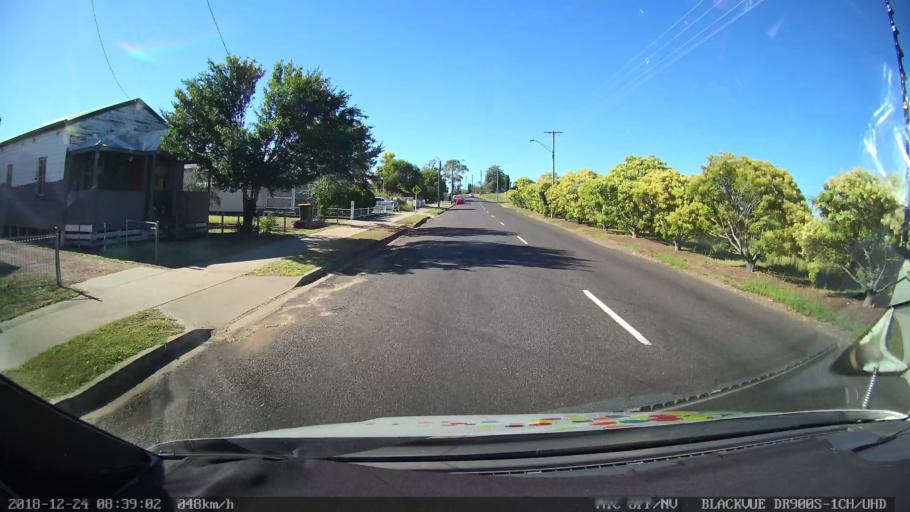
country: AU
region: New South Wales
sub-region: Liverpool Plains
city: Quirindi
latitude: -31.3452
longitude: 150.6474
